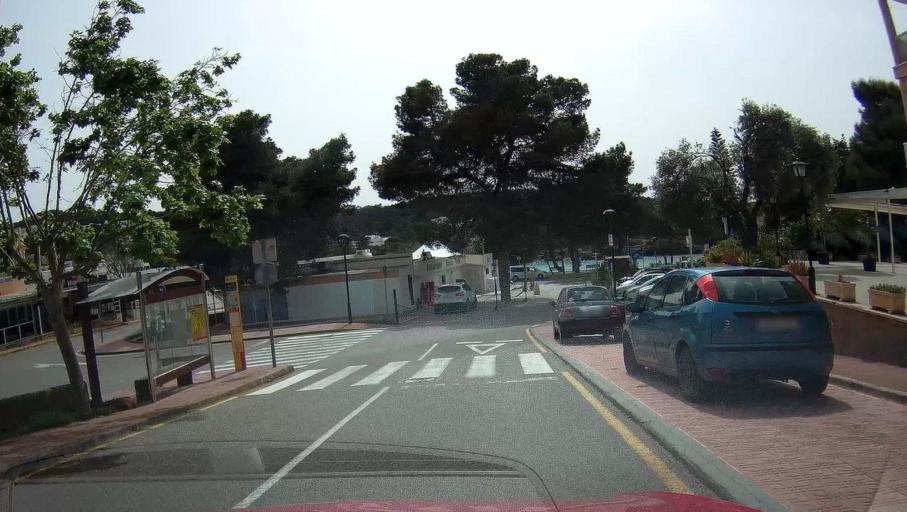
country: ES
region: Balearic Islands
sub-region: Illes Balears
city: Sant Joan de Labritja
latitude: 39.1109
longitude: 1.5186
